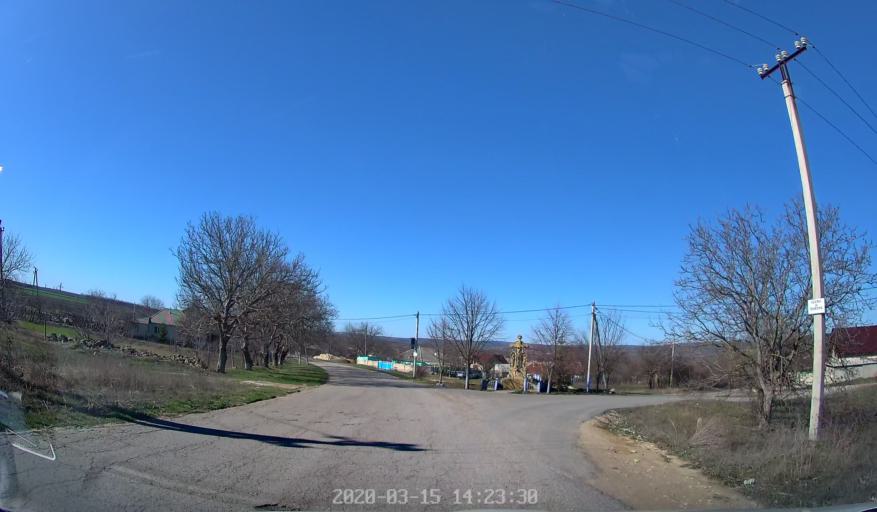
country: MD
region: Orhei
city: Orhei
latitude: 47.3305
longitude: 28.9240
